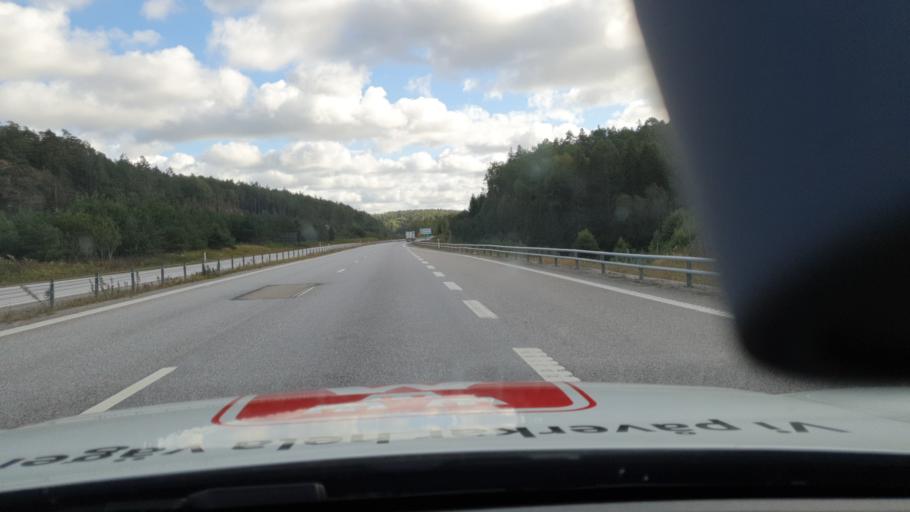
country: SE
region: Vaestra Goetaland
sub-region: Stromstads Kommun
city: Stroemstad
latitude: 59.0193
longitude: 11.2389
